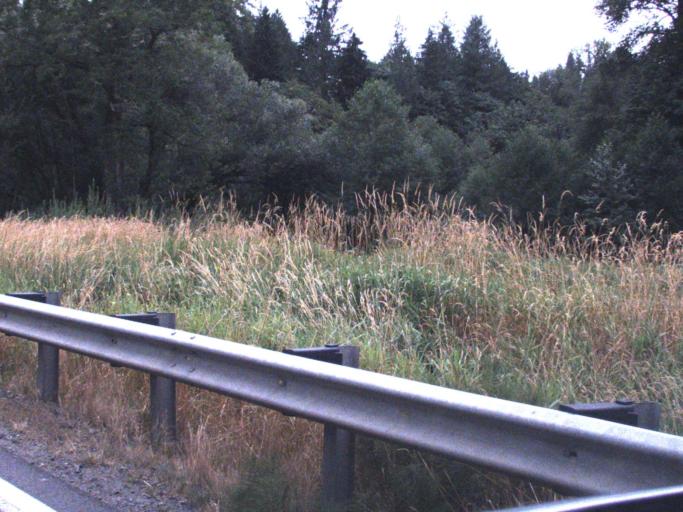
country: US
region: Washington
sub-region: King County
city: Lake Marcel-Stillwater
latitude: 47.6776
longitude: -121.9070
